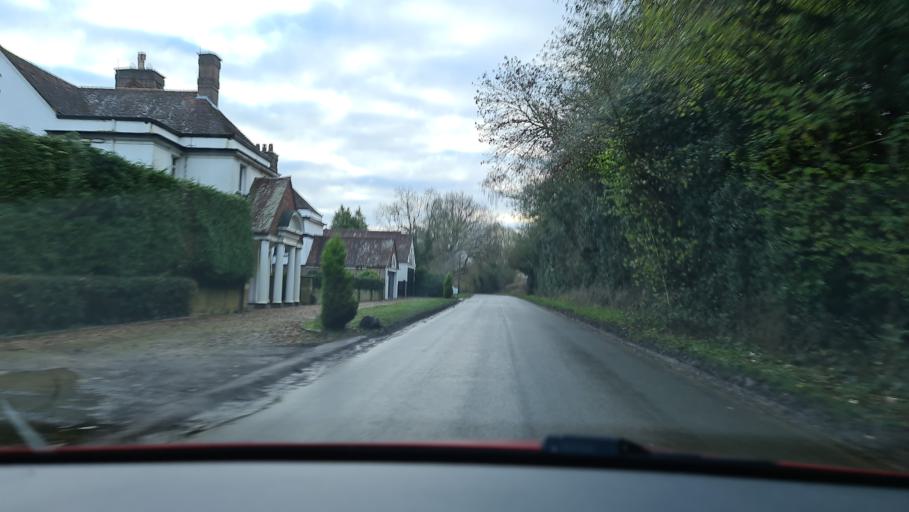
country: GB
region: England
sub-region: Buckinghamshire
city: Great Missenden
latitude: 51.7304
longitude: -0.6630
